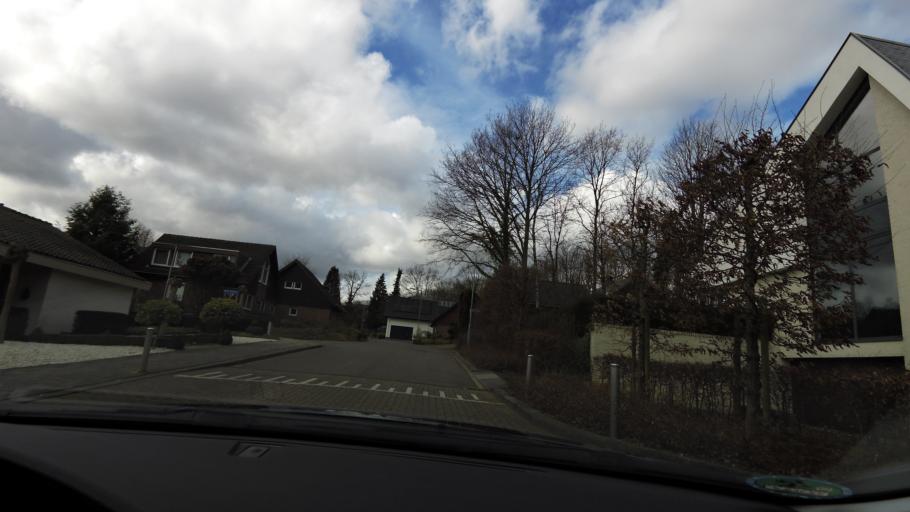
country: NL
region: Limburg
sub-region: Gemeente Nuth
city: Nuth
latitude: 50.9077
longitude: 5.8813
